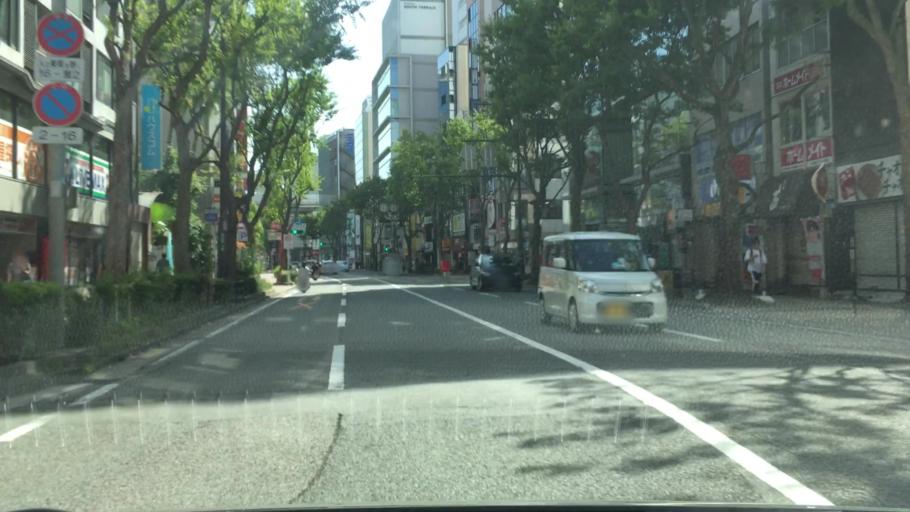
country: JP
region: Fukuoka
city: Fukuoka-shi
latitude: 33.5866
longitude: 130.3981
